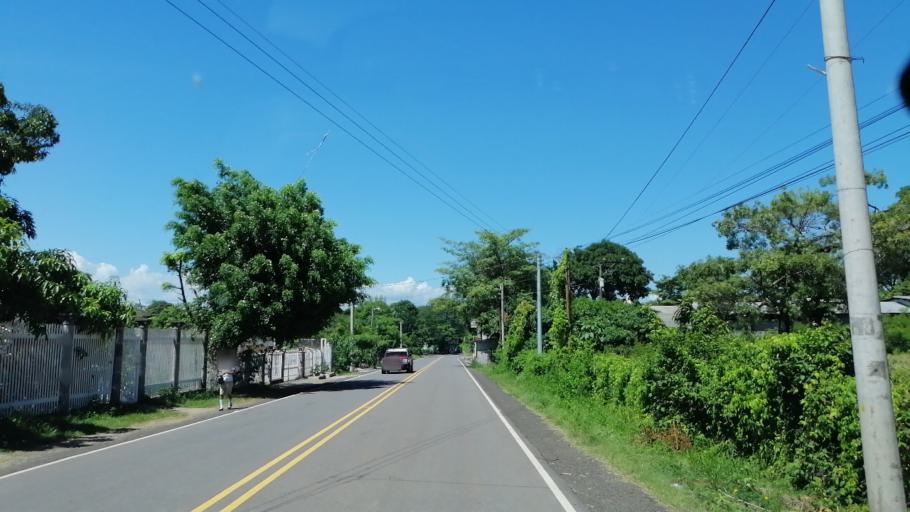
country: SV
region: San Miguel
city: Ciudad Barrios
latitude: 13.8141
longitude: -88.1751
